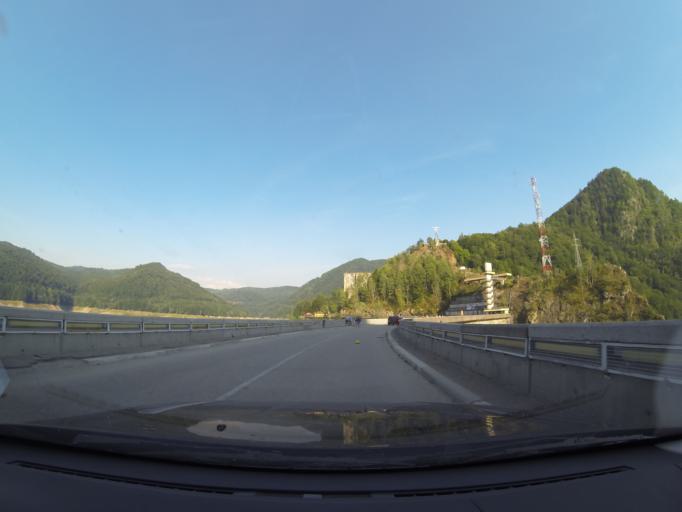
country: RO
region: Arges
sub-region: Comuna Arefu
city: Arefu
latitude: 45.3635
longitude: 24.6364
